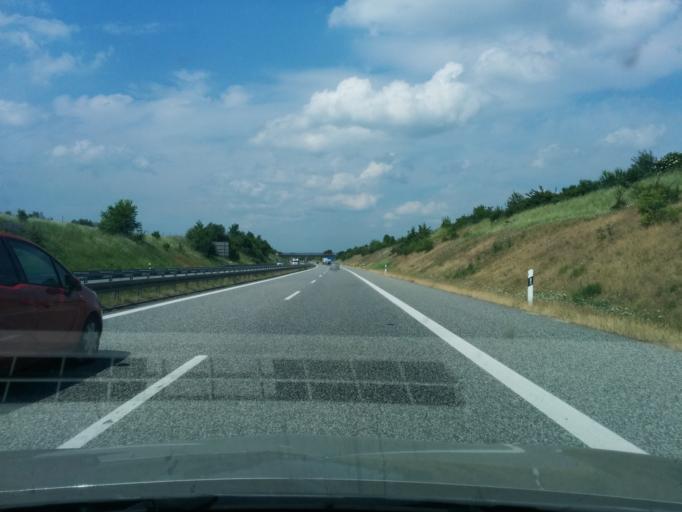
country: DE
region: Mecklenburg-Vorpommern
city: Pasewalk
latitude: 53.4659
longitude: 13.9625
